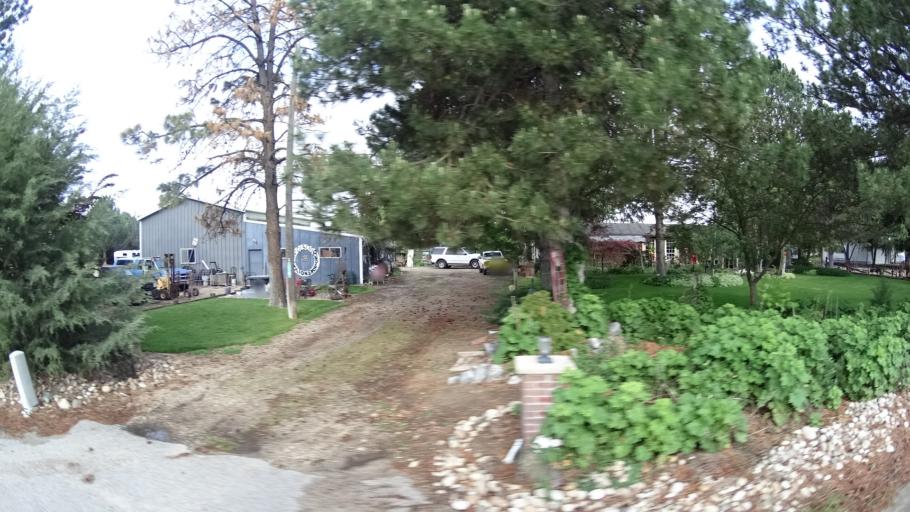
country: US
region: Idaho
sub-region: Ada County
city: Star
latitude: 43.7114
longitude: -116.5126
